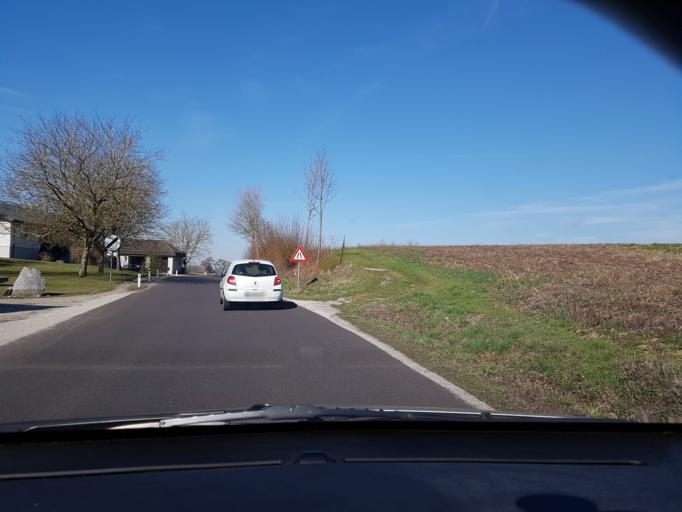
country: AT
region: Upper Austria
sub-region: Politischer Bezirk Linz-Land
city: Ansfelden
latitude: 48.2039
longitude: 14.3078
